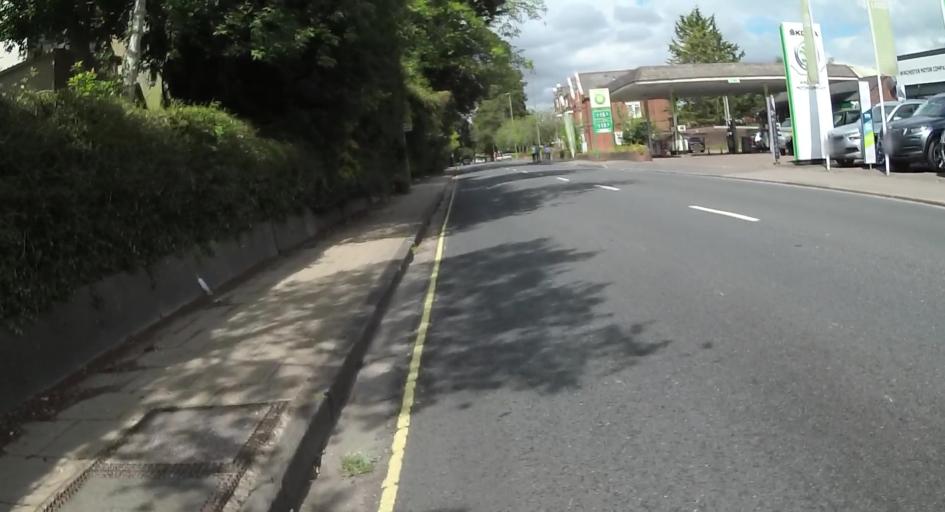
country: GB
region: England
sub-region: Hampshire
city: Winchester
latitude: 51.0535
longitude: -1.3211
